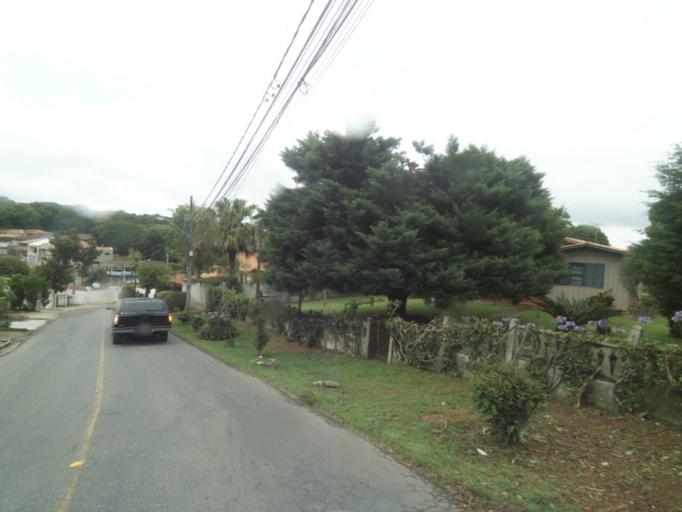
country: BR
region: Parana
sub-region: Curitiba
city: Curitiba
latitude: -25.4216
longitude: -49.3363
